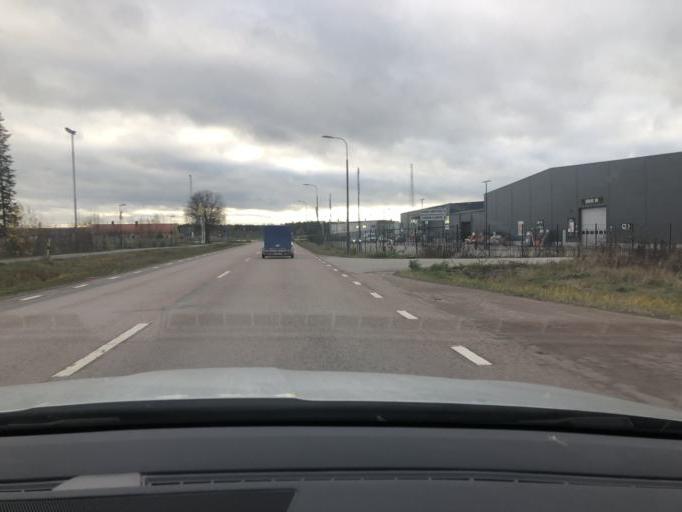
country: SE
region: Uppsala
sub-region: Tierps Kommun
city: Tierp
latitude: 60.3472
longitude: 17.4941
